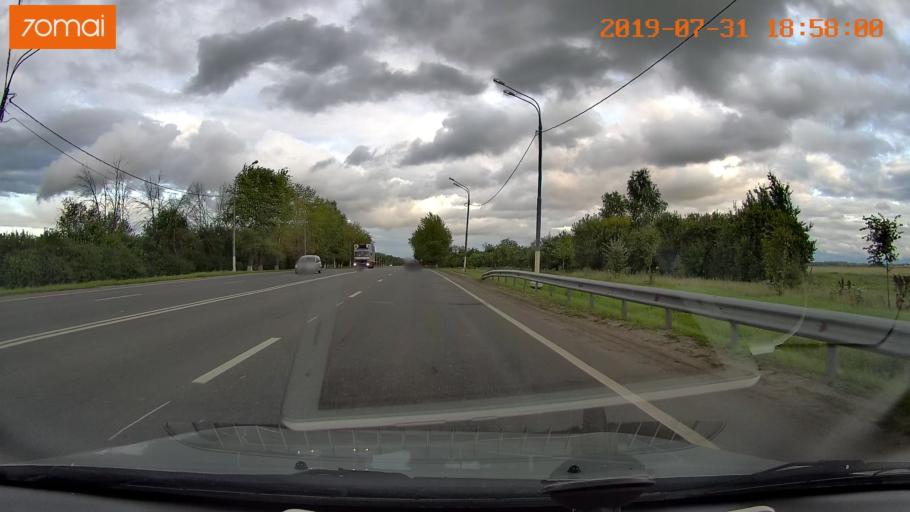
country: RU
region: Moskovskaya
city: Raduzhnyy
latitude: 55.1499
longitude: 38.6991
